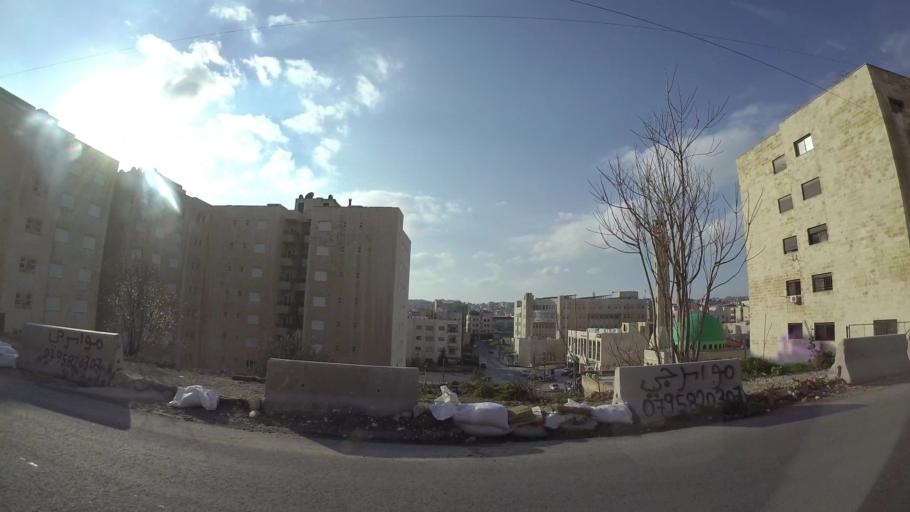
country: JO
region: Amman
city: Al Jubayhah
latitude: 31.9850
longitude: 35.8699
